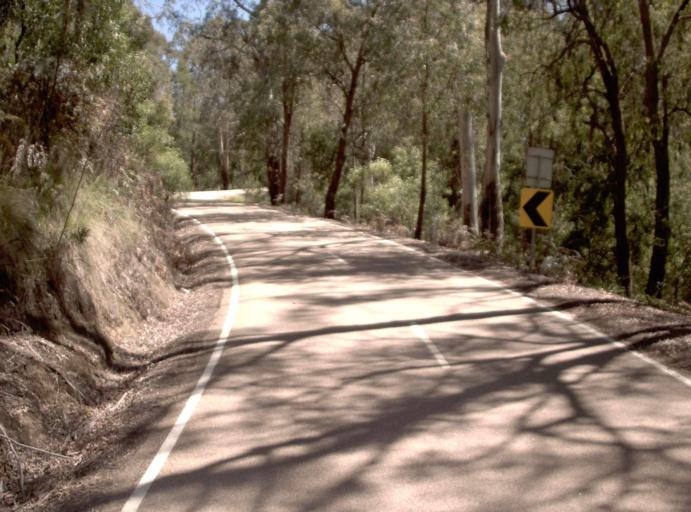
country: AU
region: Victoria
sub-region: East Gippsland
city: Lakes Entrance
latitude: -37.2243
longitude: 148.2637
